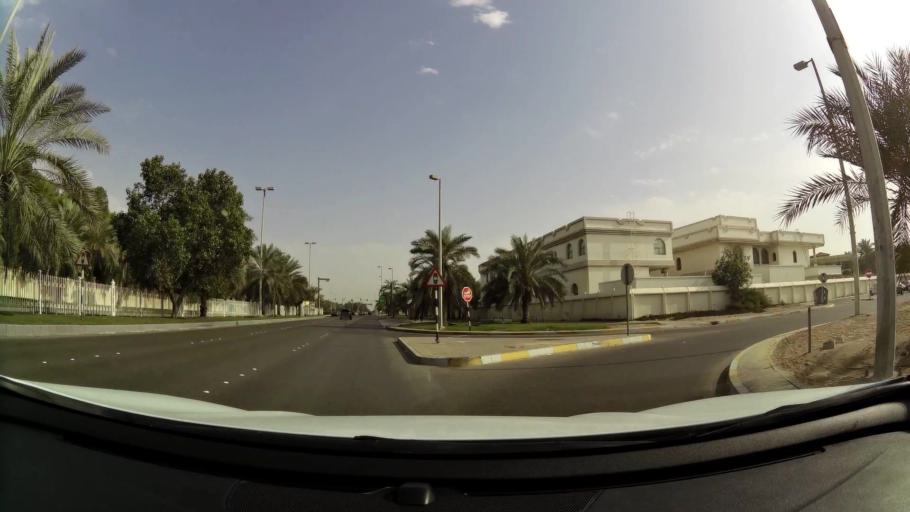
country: AE
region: Abu Dhabi
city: Abu Dhabi
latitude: 24.4692
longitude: 54.3537
